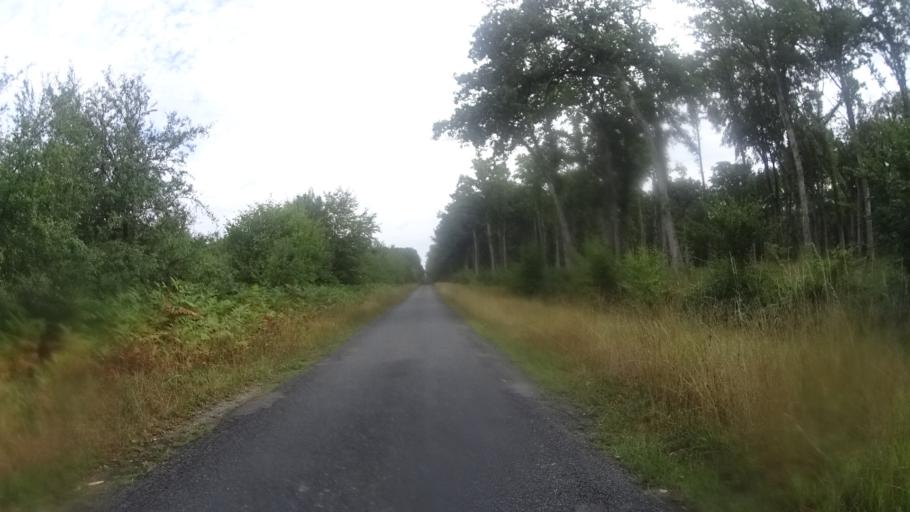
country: FR
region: Centre
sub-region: Departement du Loiret
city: Vitry-aux-Loges
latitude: 48.0118
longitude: 2.2454
